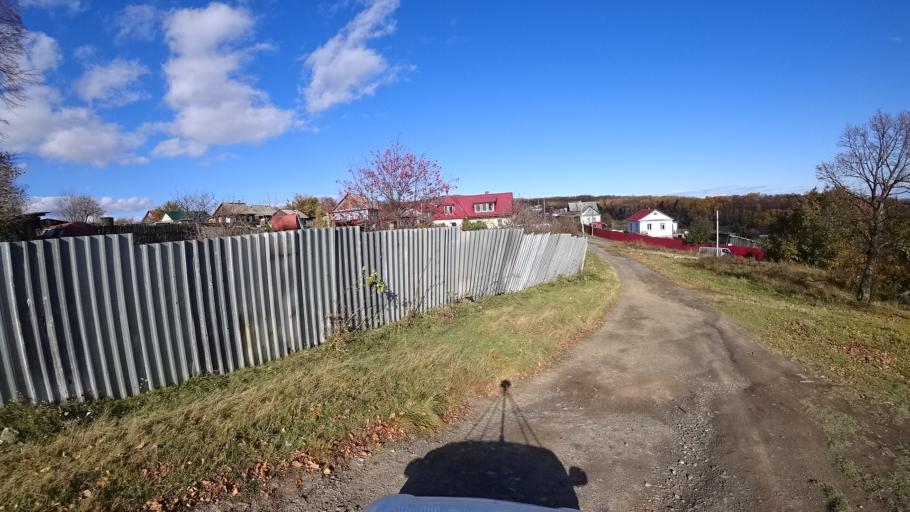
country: RU
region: Khabarovsk Krai
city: Amursk
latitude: 50.2306
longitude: 136.9172
